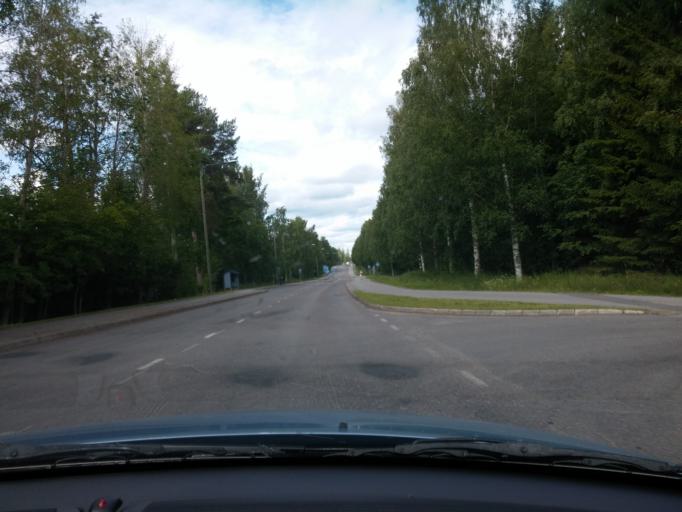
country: FI
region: Central Finland
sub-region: Saarijaervi-Viitasaari
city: Saarijaervi
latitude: 62.7075
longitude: 25.2262
